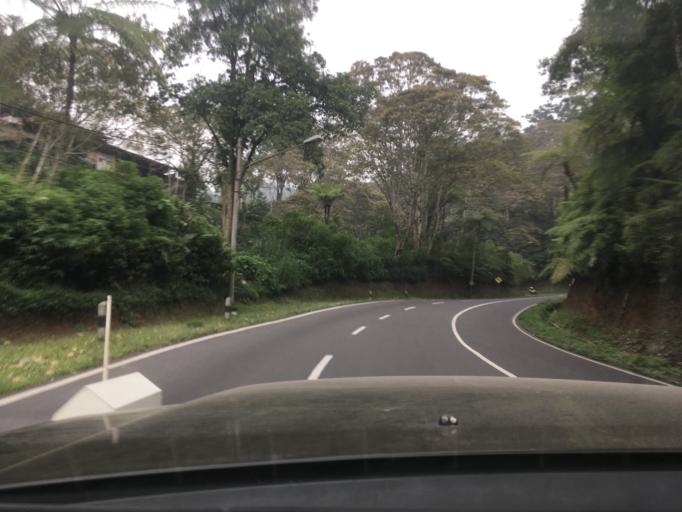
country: ID
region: West Java
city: Lembang
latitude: -6.7695
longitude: 107.6368
